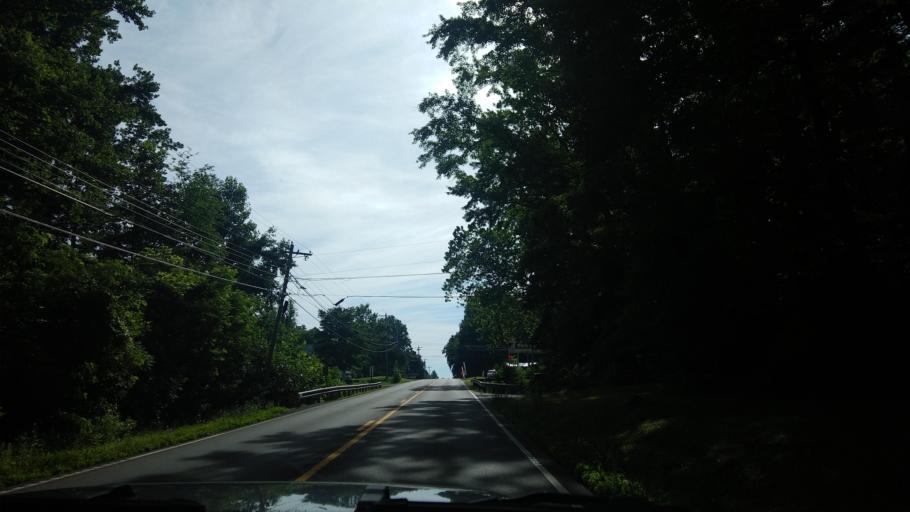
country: US
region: Tennessee
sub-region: Cocke County
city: Newport
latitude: 35.7670
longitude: -83.2866
